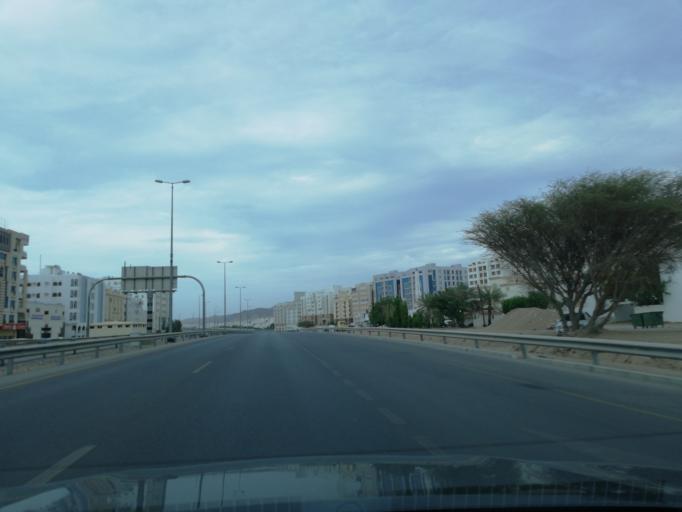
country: OM
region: Muhafazat Masqat
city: Bawshar
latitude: 23.5852
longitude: 58.4232
